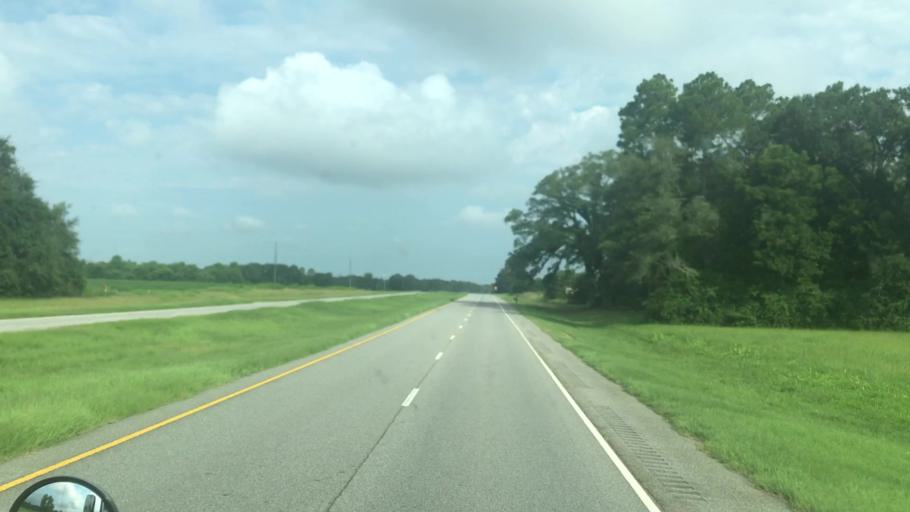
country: US
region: Georgia
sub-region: Miller County
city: Colquitt
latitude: 31.2668
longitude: -84.8205
